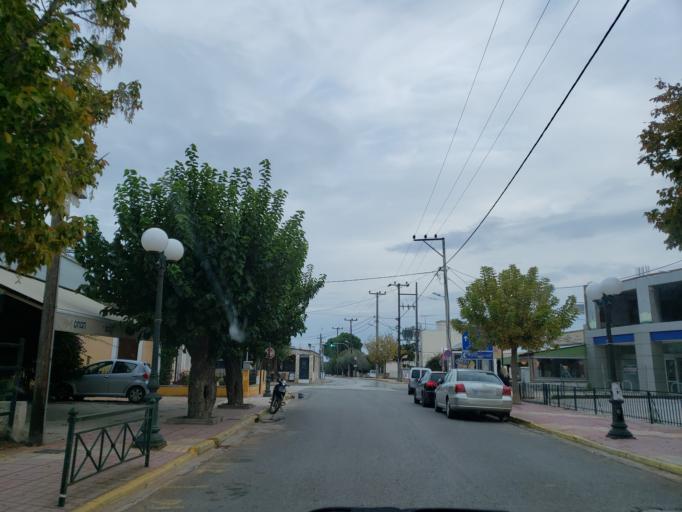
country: GR
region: Attica
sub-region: Nomarchia Anatolikis Attikis
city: Marathonas
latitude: 38.1536
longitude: 23.9617
